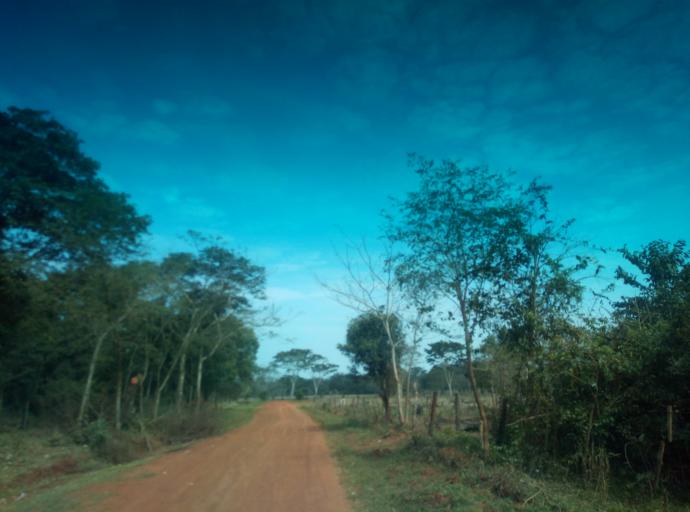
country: PY
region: Caaguazu
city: Carayao
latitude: -25.1966
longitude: -56.2520
